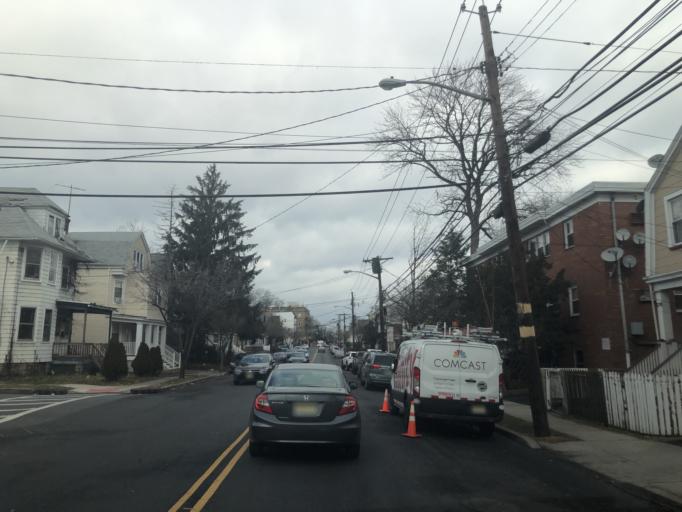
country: US
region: New Jersey
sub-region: Essex County
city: Irvington
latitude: 40.7269
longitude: -74.2365
